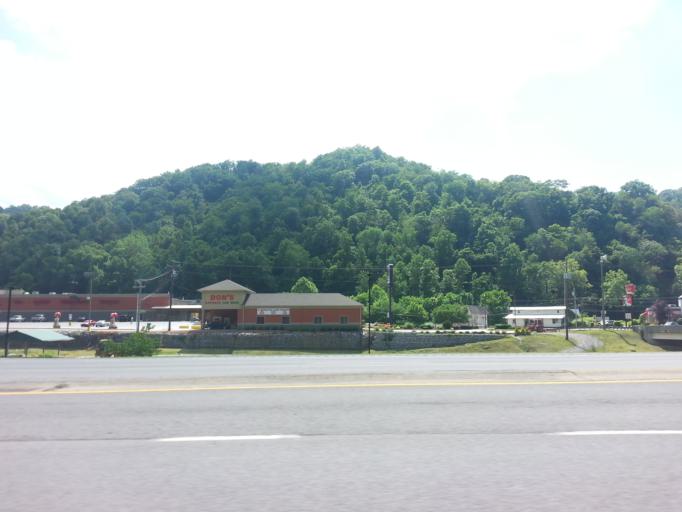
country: US
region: Kentucky
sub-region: Harlan County
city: Harlan
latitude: 36.8206
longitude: -83.3174
